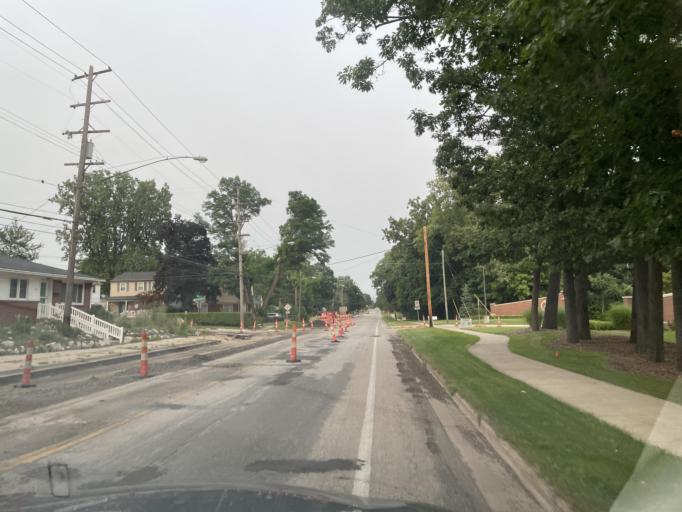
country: US
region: Michigan
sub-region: Kent County
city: East Grand Rapids
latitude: 42.9627
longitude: -85.6294
